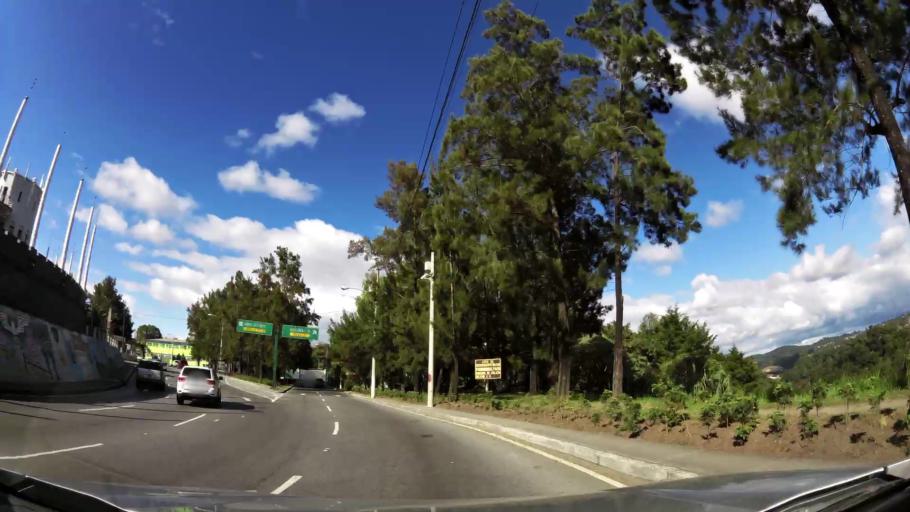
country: GT
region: Guatemala
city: Guatemala City
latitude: 14.6134
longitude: -90.5041
